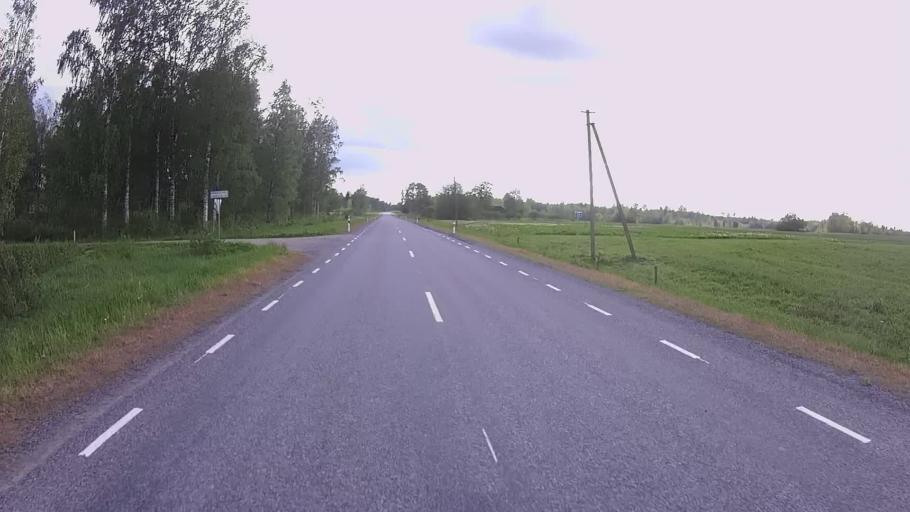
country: EE
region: Jogevamaa
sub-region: Mustvee linn
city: Mustvee
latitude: 59.0168
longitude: 26.9474
